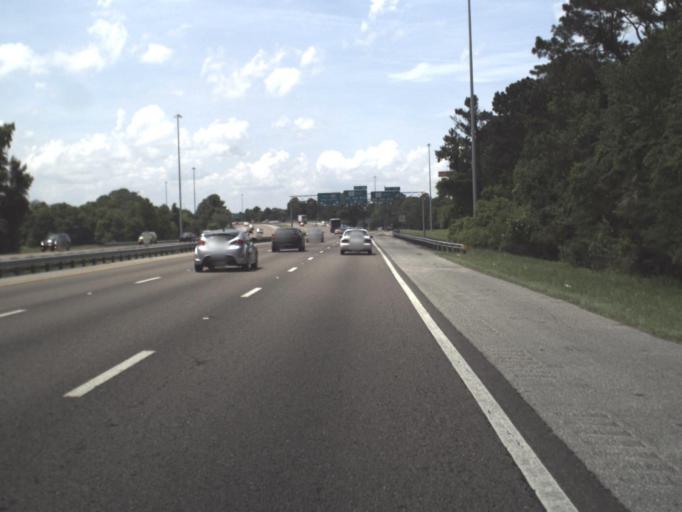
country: US
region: Florida
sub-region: Saint Johns County
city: Fruit Cove
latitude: 30.1781
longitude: -81.6227
